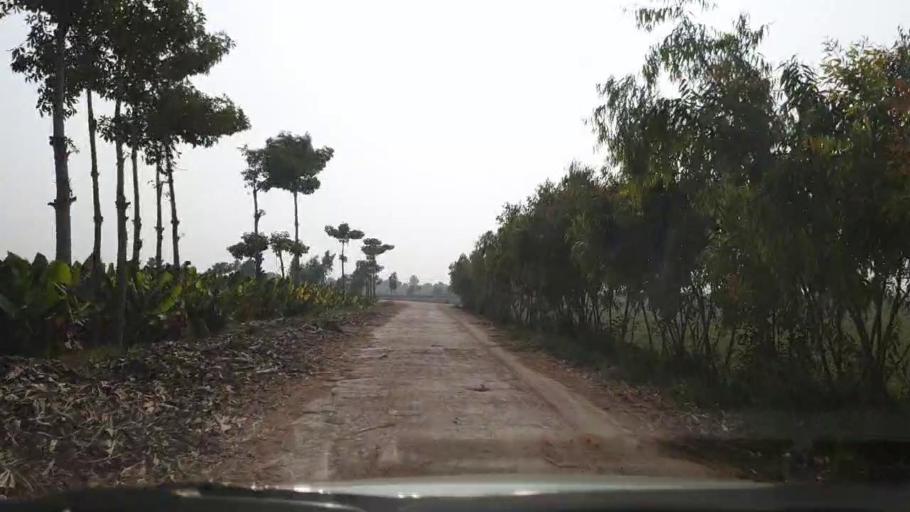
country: PK
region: Sindh
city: Matiari
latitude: 25.6548
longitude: 68.5502
